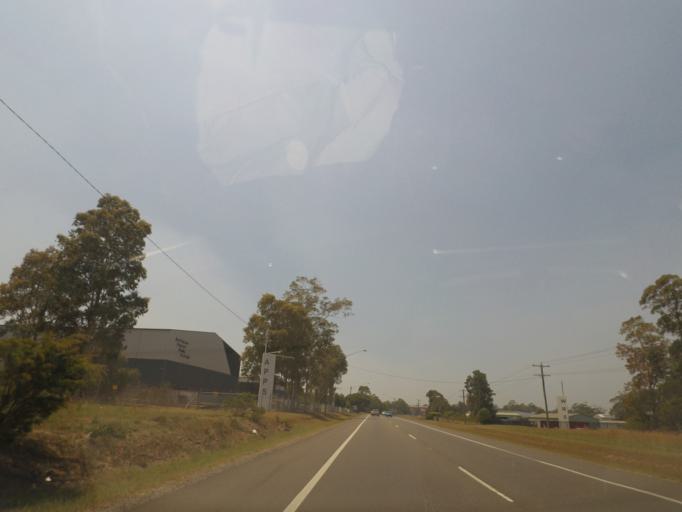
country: AU
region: New South Wales
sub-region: Newcastle
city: Beresfield
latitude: -32.8228
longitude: 151.7031
